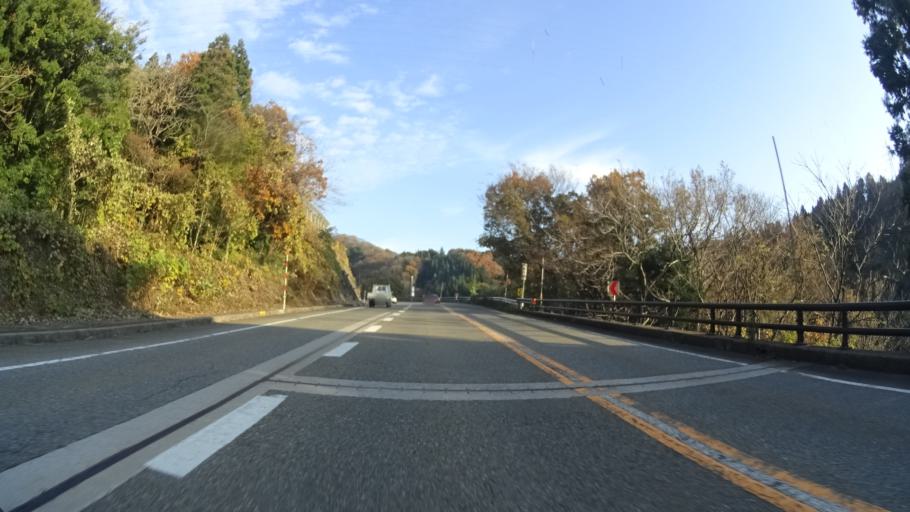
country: JP
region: Niigata
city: Kashiwazaki
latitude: 37.4058
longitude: 138.6544
